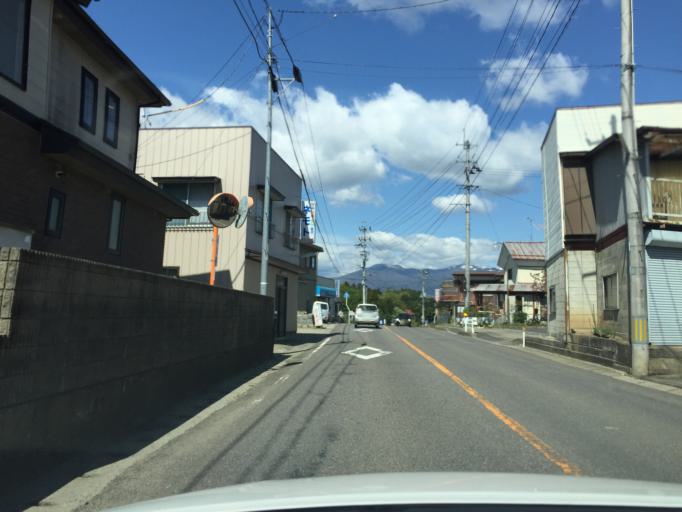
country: JP
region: Fukushima
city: Nihommatsu
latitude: 37.5757
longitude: 140.4629
